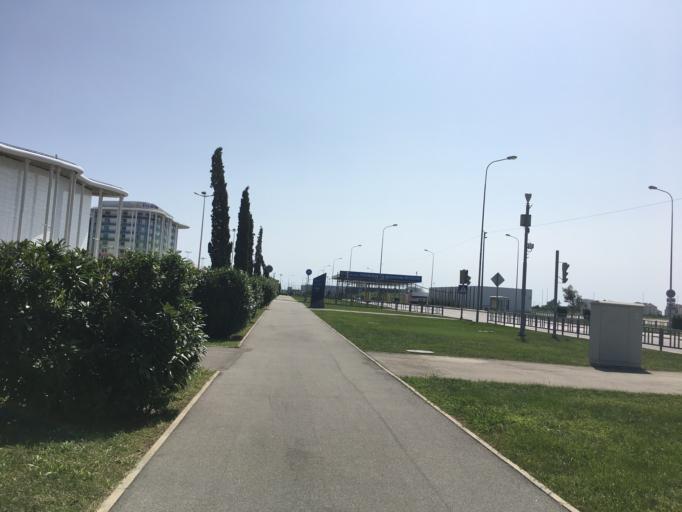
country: RU
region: Krasnodarskiy
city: Adler
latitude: 43.4141
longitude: 39.9483
